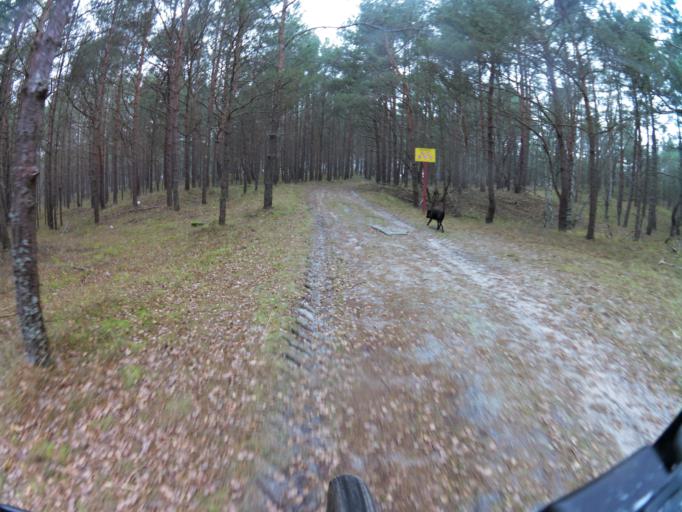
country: PL
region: West Pomeranian Voivodeship
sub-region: Powiat gryficki
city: Cerkwica
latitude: 54.1112
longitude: 15.1494
